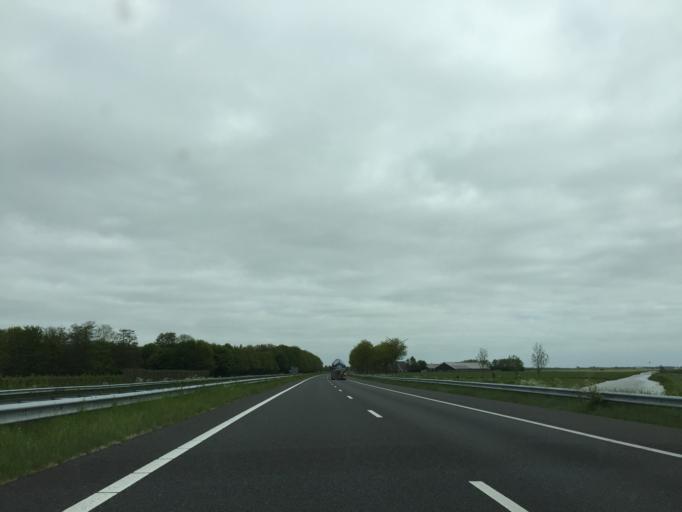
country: NL
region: North Holland
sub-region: Gemeente Medemblik
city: Opperdoes
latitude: 52.7275
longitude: 5.0258
